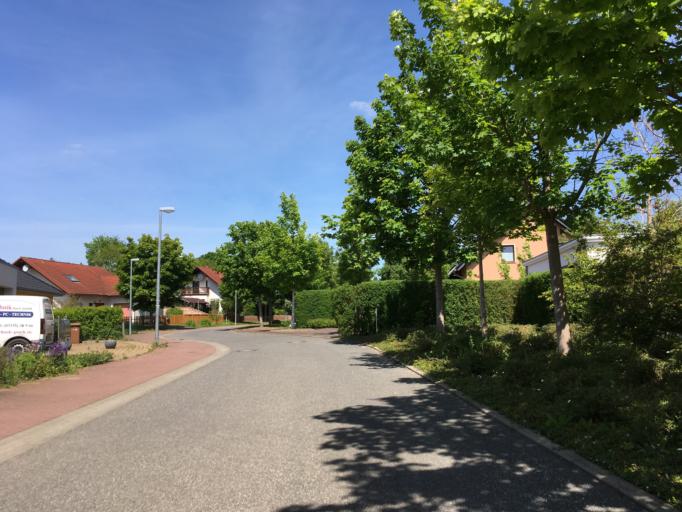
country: DE
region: Brandenburg
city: Eberswalde
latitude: 52.8413
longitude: 13.8274
